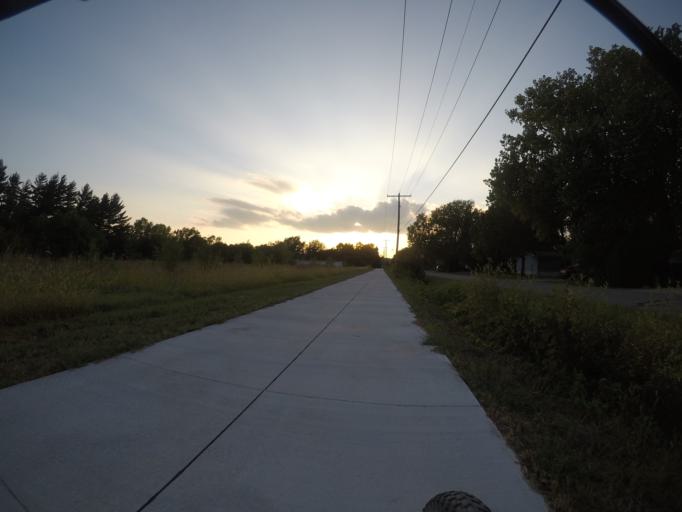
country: US
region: Kansas
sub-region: Riley County
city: Manhattan
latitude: 39.2040
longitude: -96.5518
